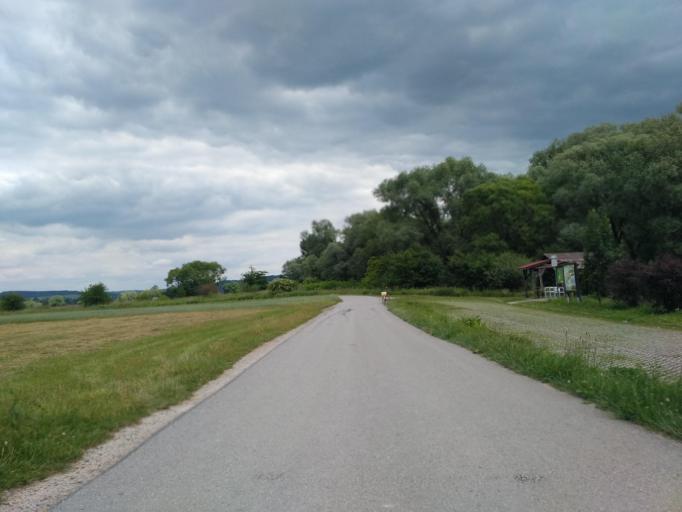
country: PL
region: Subcarpathian Voivodeship
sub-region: Powiat rzeszowski
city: Dynow
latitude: 49.8119
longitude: 22.2462
